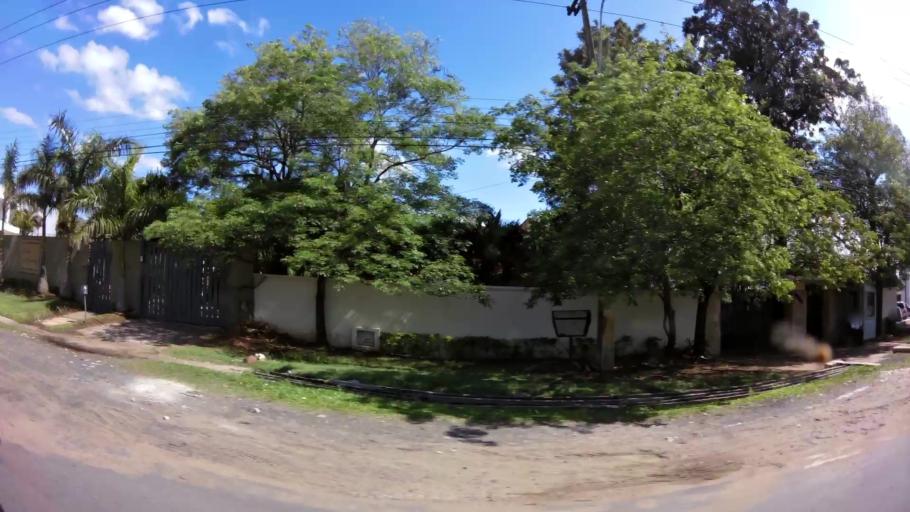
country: PY
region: Central
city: Fernando de la Mora
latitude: -25.2810
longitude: -57.5371
